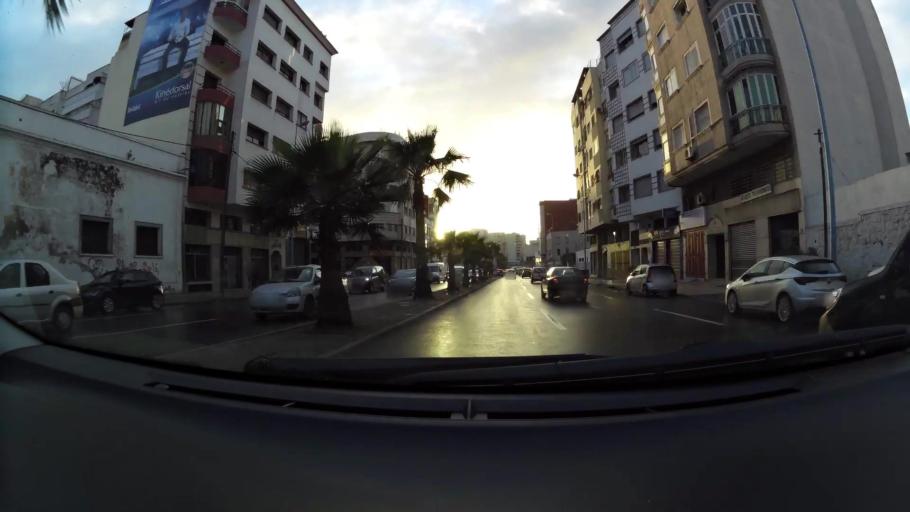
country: MA
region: Grand Casablanca
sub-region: Casablanca
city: Casablanca
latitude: 33.5873
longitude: -7.5962
